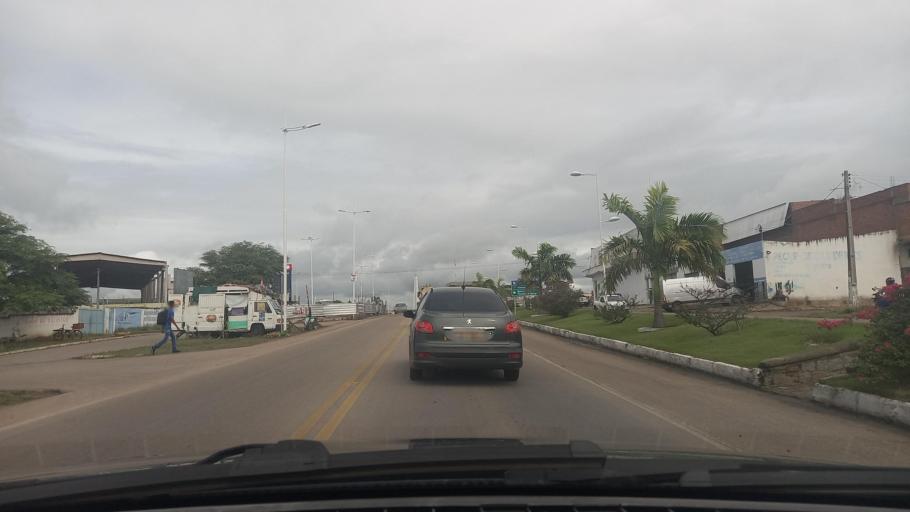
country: BR
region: Bahia
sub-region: Paulo Afonso
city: Paulo Afonso
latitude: -9.4450
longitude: -38.2223
